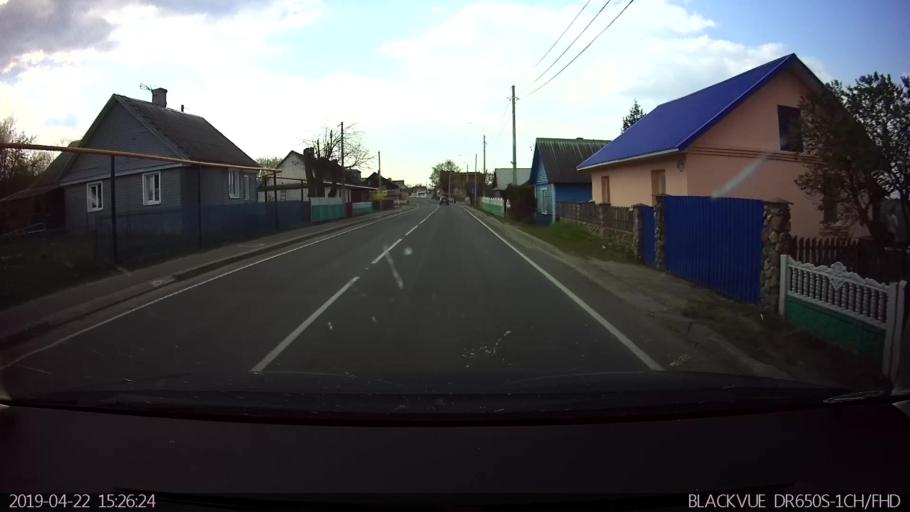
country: BY
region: Brest
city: Vysokaye
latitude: 52.3677
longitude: 23.3822
